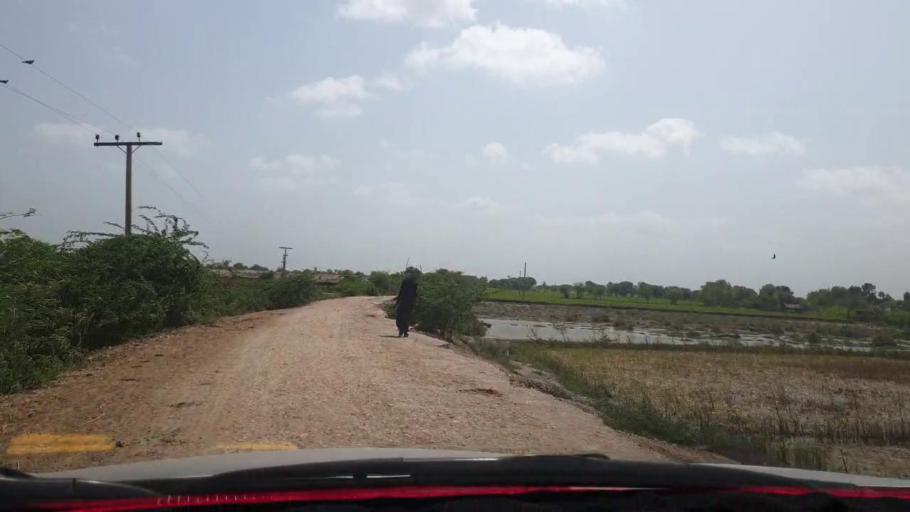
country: PK
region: Sindh
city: Talhar
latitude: 24.8998
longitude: 68.9060
